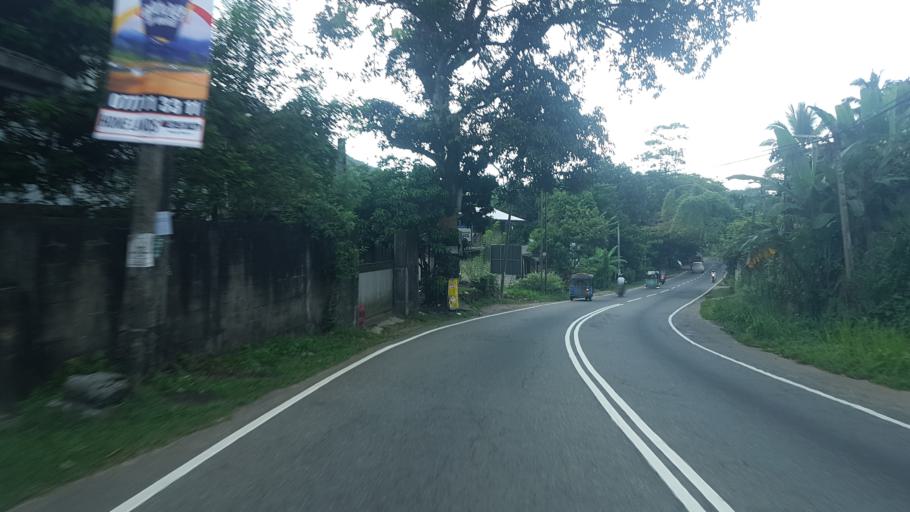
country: LK
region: Western
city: Hanwella Ihala
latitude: 7.0048
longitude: 80.2621
